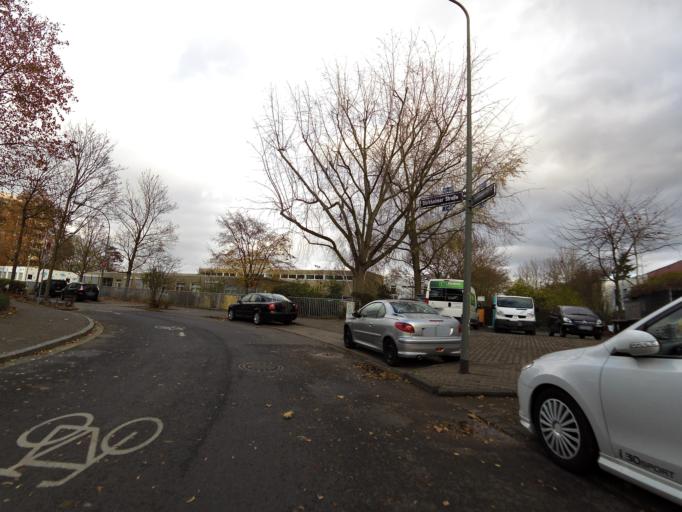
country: DE
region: Hesse
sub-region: Regierungsbezirk Darmstadt
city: Eschborn
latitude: 50.0978
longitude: 8.5782
